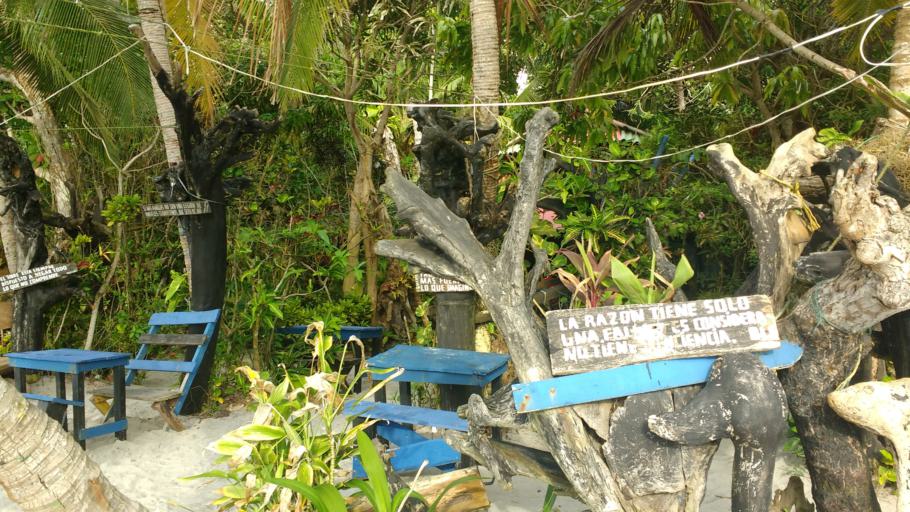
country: CO
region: Antioquia
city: Necocli
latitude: 8.4466
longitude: -76.7959
